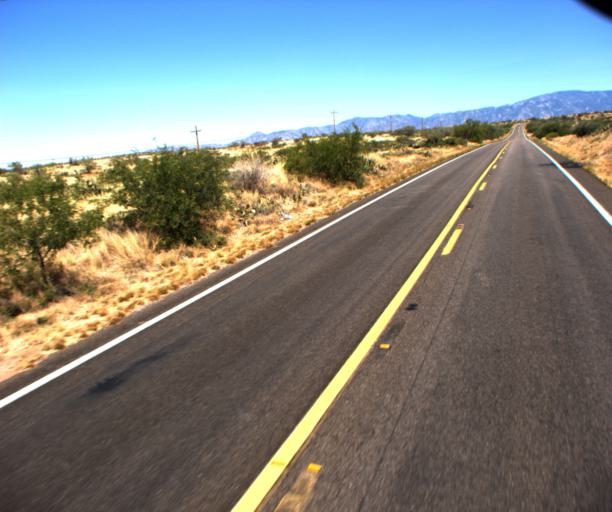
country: US
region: Arizona
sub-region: Pima County
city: Catalina
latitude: 32.6216
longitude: -110.9952
